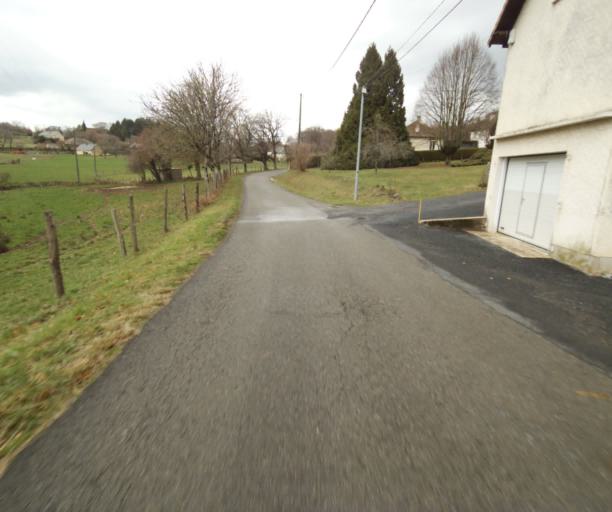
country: FR
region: Limousin
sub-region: Departement de la Correze
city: Saint-Mexant
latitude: 45.2857
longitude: 1.6345
